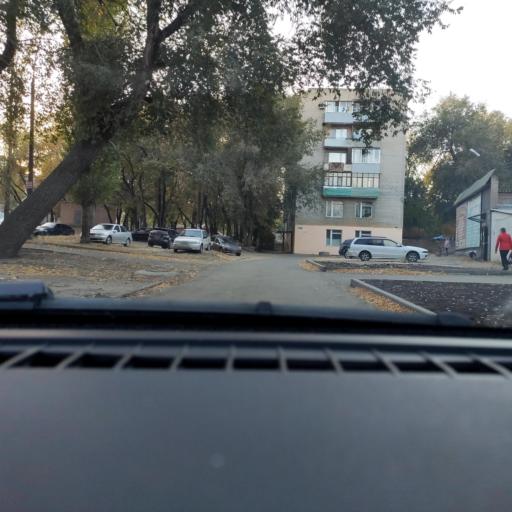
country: RU
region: Voronezj
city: Maslovka
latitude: 51.6129
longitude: 39.2492
